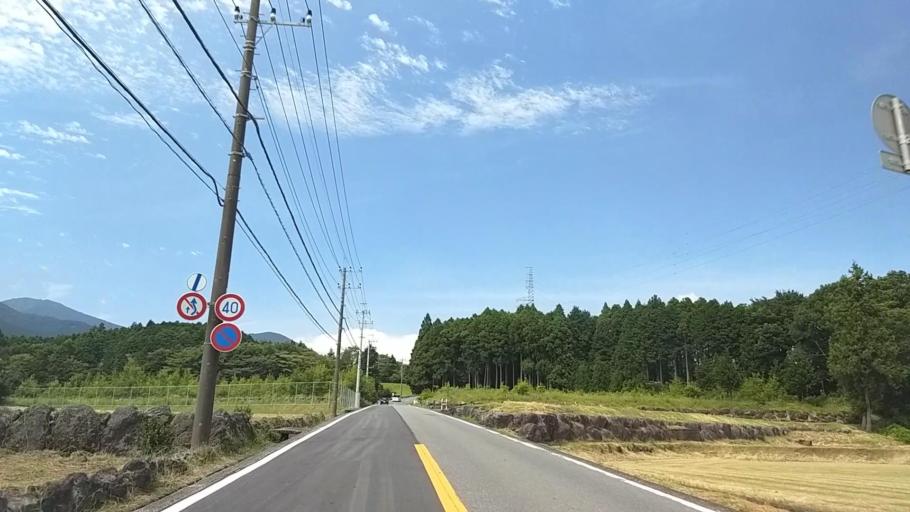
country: JP
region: Shizuoka
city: Gotemba
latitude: 35.2397
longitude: 138.8734
